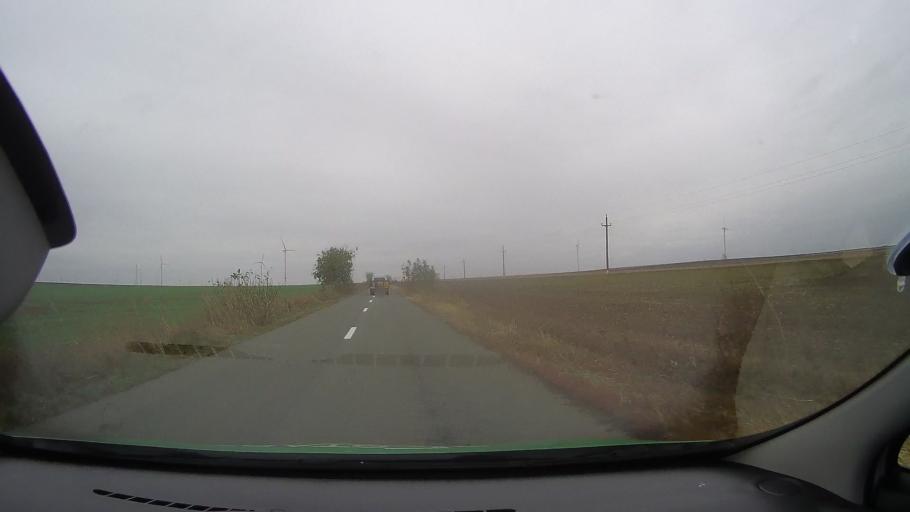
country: RO
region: Constanta
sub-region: Comuna Targusor
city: Targusor
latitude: 44.4722
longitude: 28.3854
